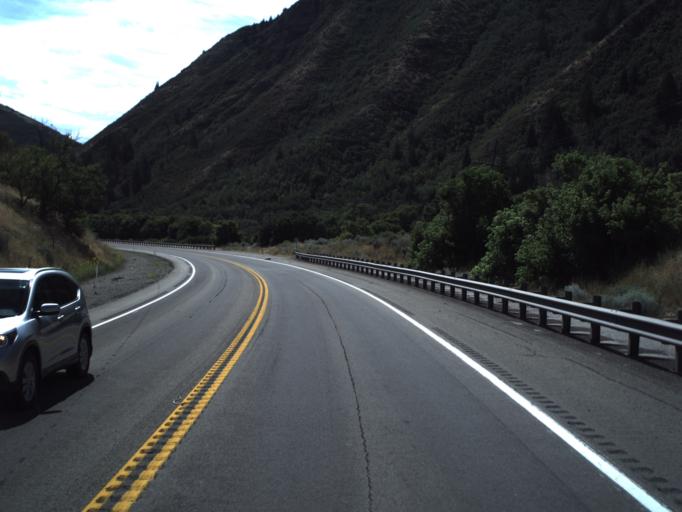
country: US
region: Utah
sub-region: Utah County
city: Mapleton
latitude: 40.0570
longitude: -111.5618
